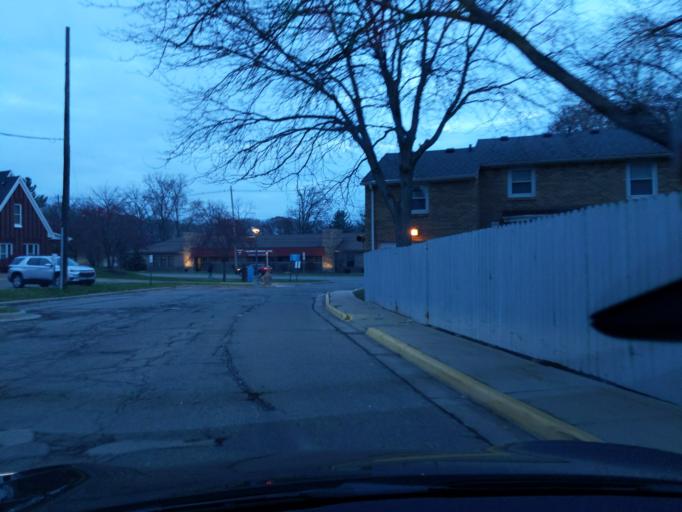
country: US
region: Michigan
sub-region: Ingham County
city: Lansing
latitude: 42.7041
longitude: -84.5580
